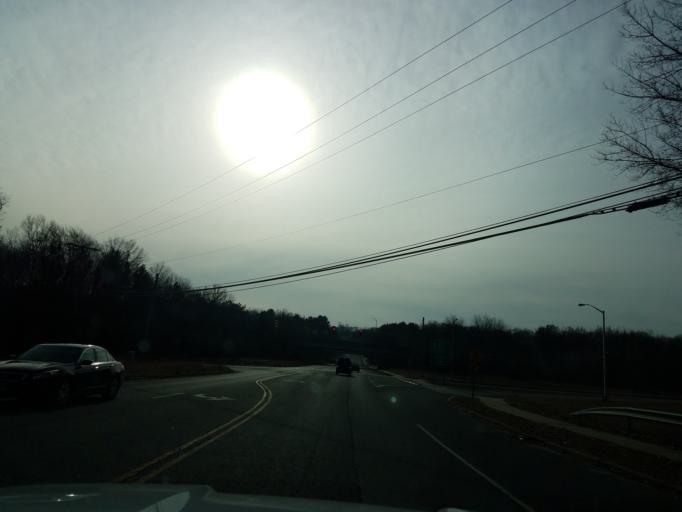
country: US
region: Connecticut
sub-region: Windham County
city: Willimantic
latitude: 41.7322
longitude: -72.2154
